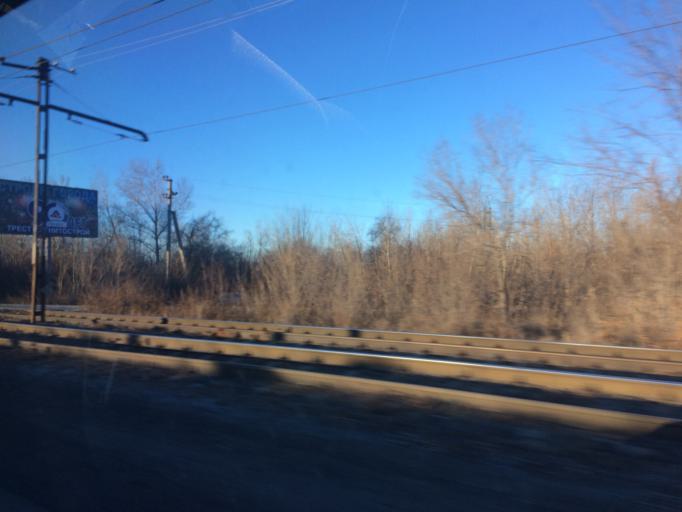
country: RU
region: Chelyabinsk
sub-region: Gorod Magnitogorsk
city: Magnitogorsk
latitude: 53.4089
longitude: 59.0312
